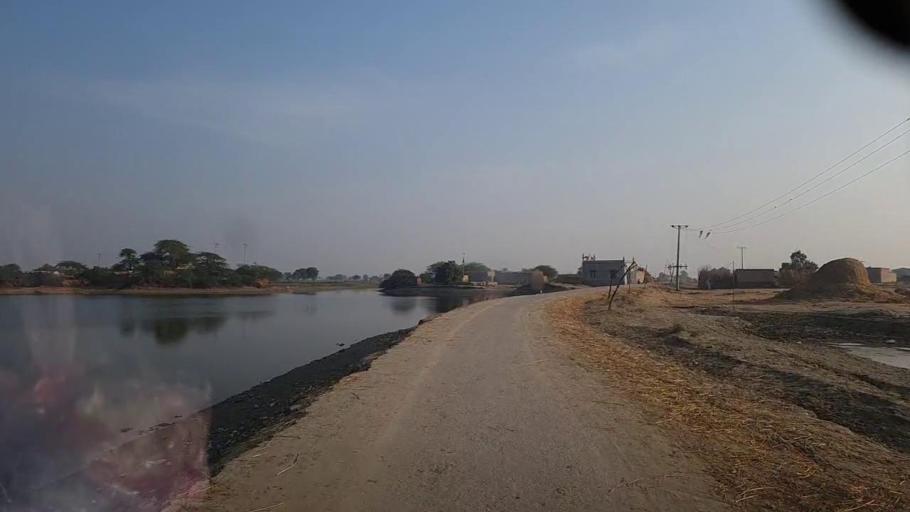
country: PK
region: Sindh
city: Jacobabad
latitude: 28.2371
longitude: 68.4838
